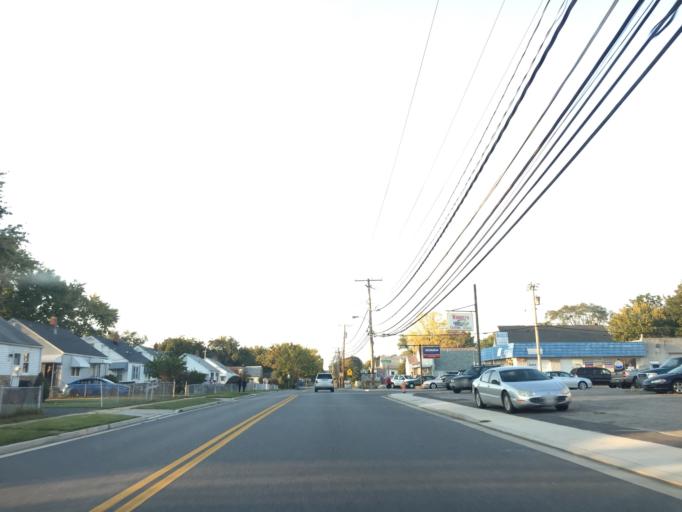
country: US
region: Maryland
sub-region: Baltimore County
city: Essex
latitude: 39.3028
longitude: -76.4627
